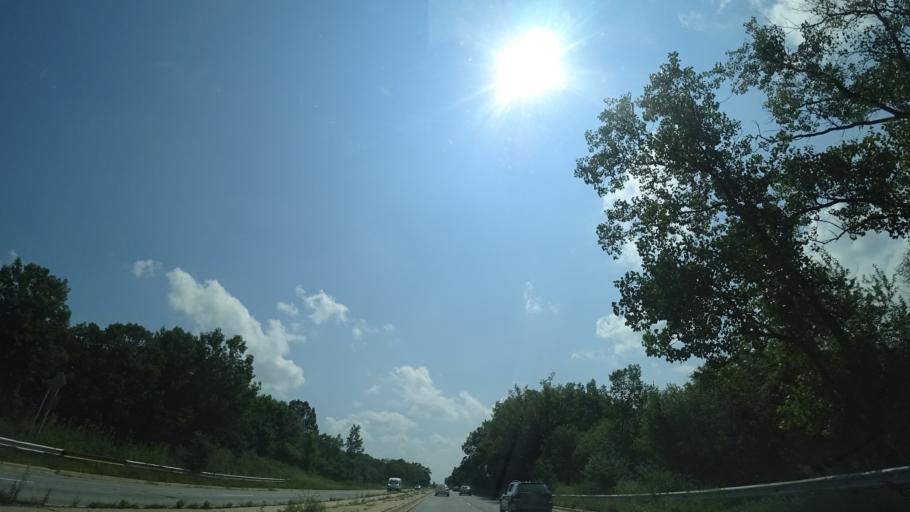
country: US
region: Illinois
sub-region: Cook County
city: Palos Heights
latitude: 41.6521
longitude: -87.7959
